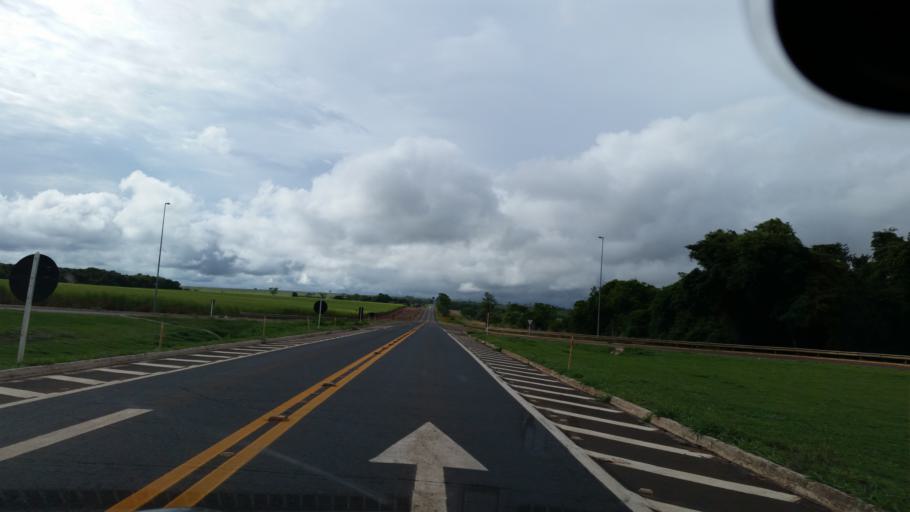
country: BR
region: Minas Gerais
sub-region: Tupaciguara
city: Tupaciguara
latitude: -18.7499
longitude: -48.6115
